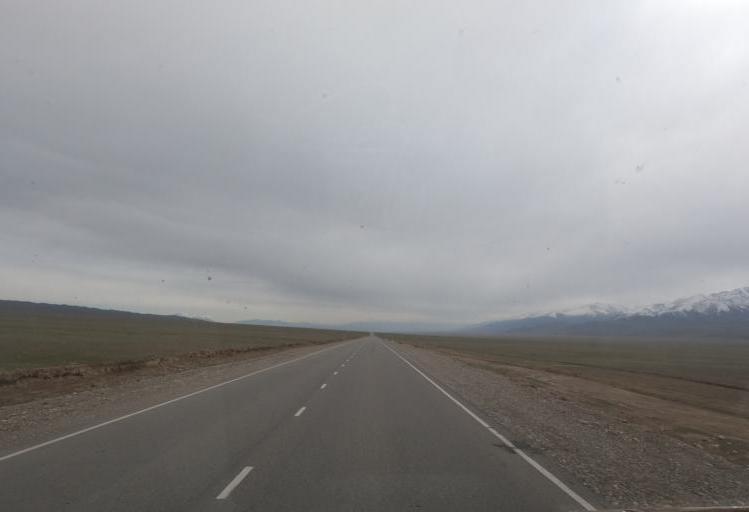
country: KG
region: Naryn
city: Baetov
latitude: 40.9773
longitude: 75.3242
